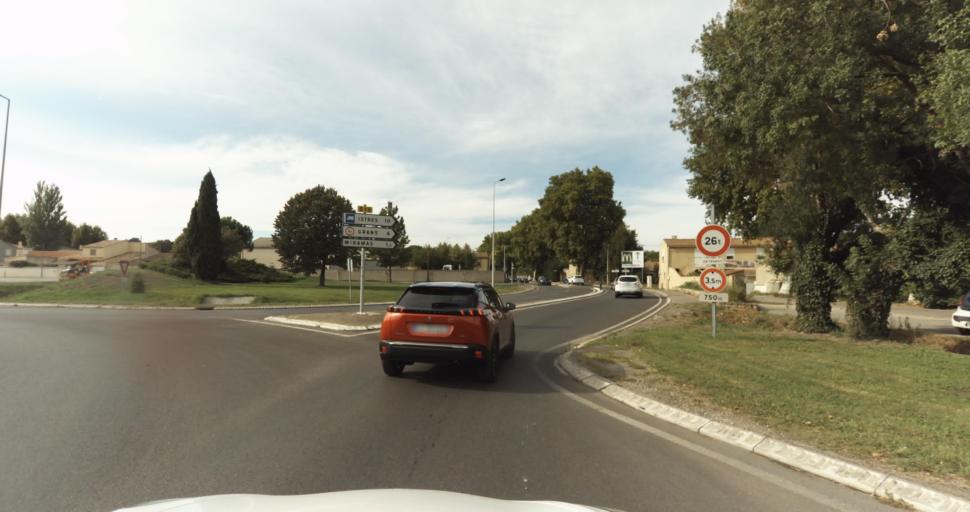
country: FR
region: Provence-Alpes-Cote d'Azur
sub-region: Departement des Bouches-du-Rhone
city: Miramas
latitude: 43.5717
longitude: 5.0190
